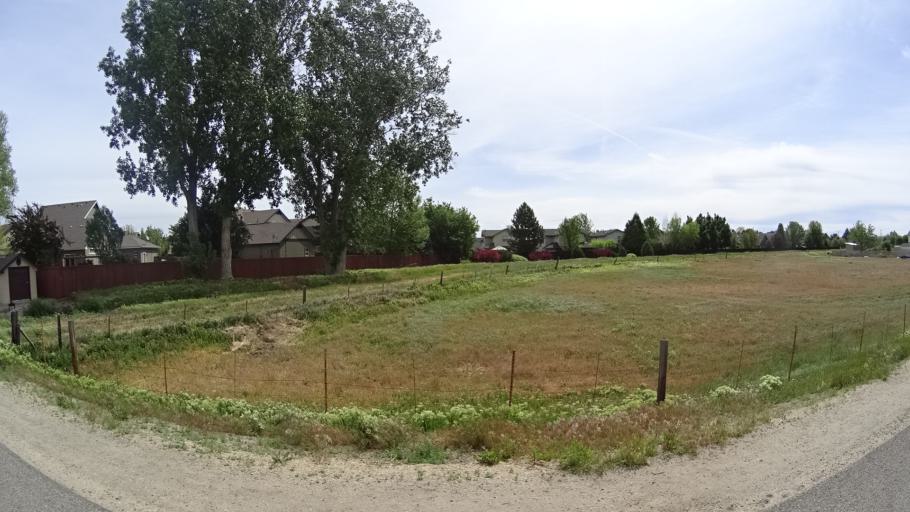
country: US
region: Idaho
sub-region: Ada County
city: Meridian
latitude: 43.5491
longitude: -116.3145
